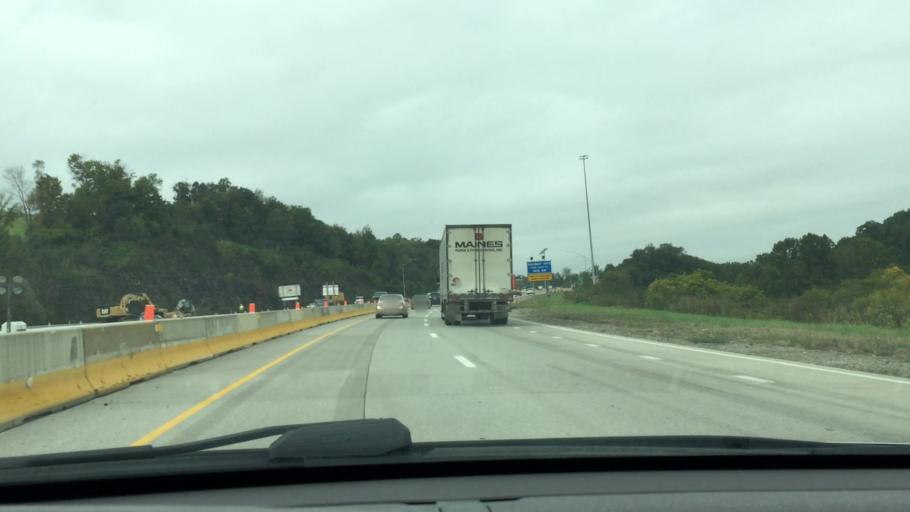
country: US
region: Pennsylvania
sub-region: Allegheny County
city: Enlow
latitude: 40.4689
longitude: -80.2043
